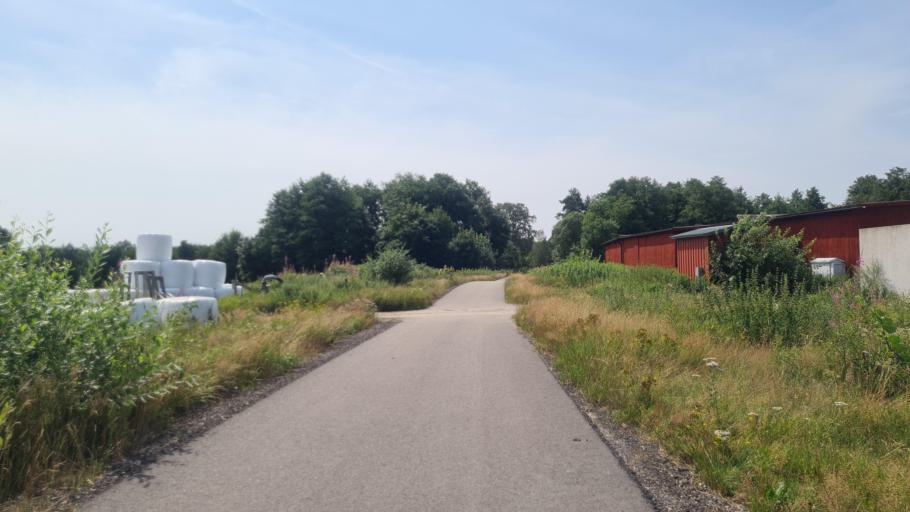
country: SE
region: Kronoberg
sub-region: Ljungby Kommun
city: Lagan
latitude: 56.8731
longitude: 13.9827
